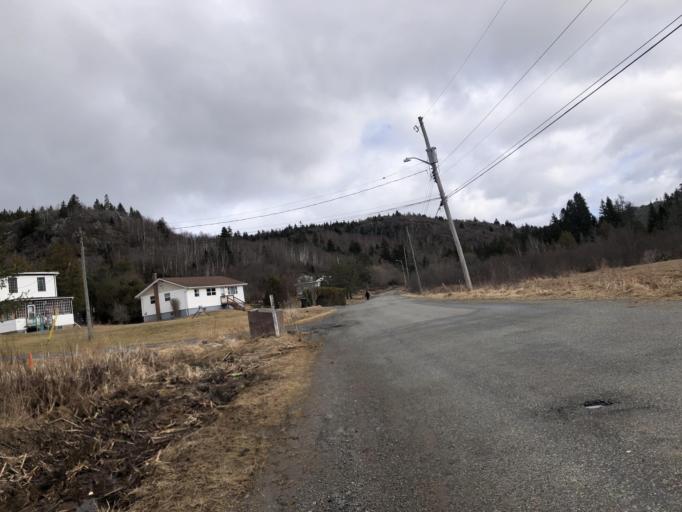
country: CA
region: New Brunswick
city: Saint John
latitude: 45.3274
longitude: -66.0121
